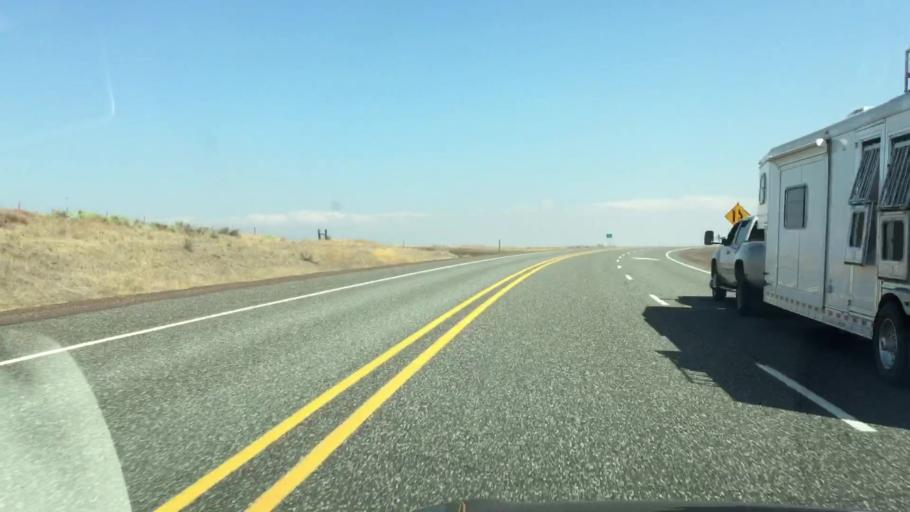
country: US
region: Oregon
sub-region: Wasco County
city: The Dalles
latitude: 45.3234
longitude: -121.1508
